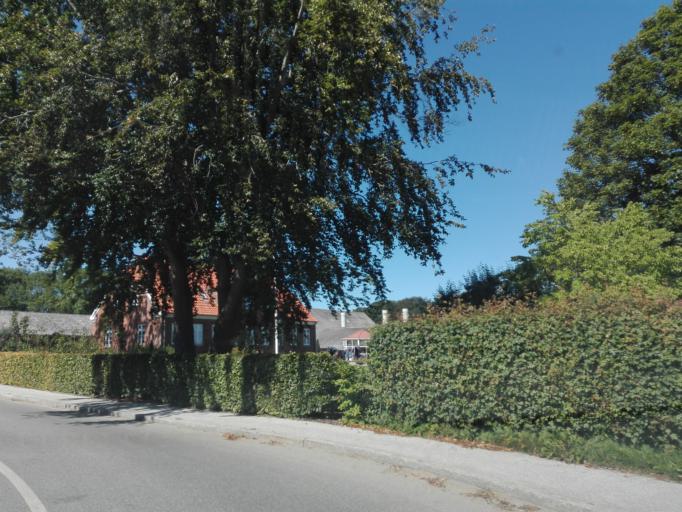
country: DK
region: Central Jutland
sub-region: Arhus Kommune
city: Beder
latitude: 56.0360
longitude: 10.2400
